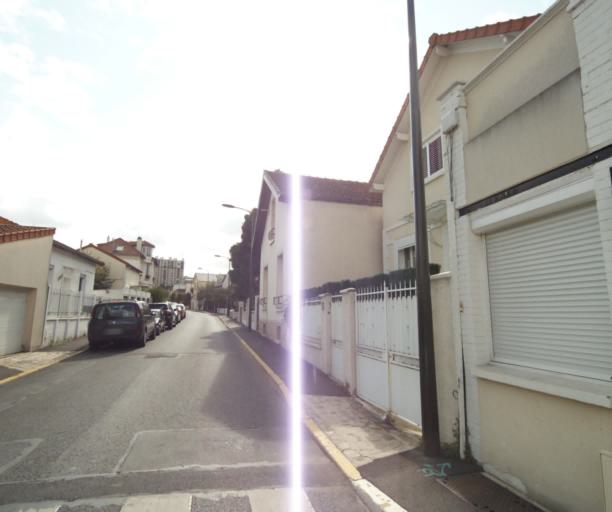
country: FR
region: Ile-de-France
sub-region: Departement des Hauts-de-Seine
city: Clamart
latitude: 48.8059
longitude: 2.2789
